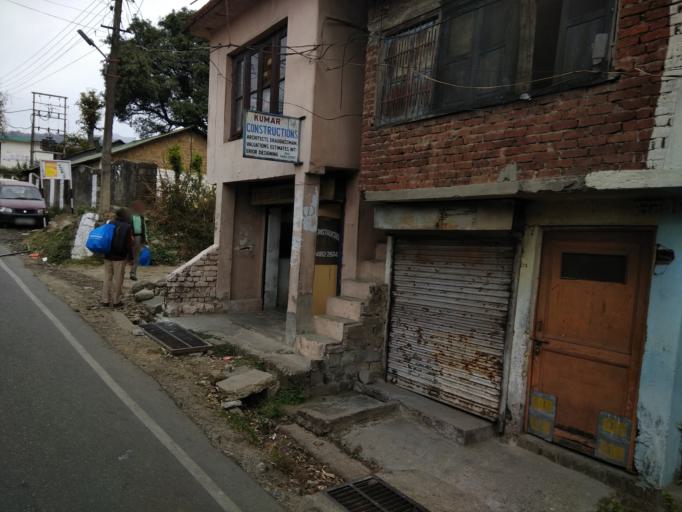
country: IN
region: Himachal Pradesh
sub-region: Kangra
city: Dharmsala
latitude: 32.2091
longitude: 76.3229
